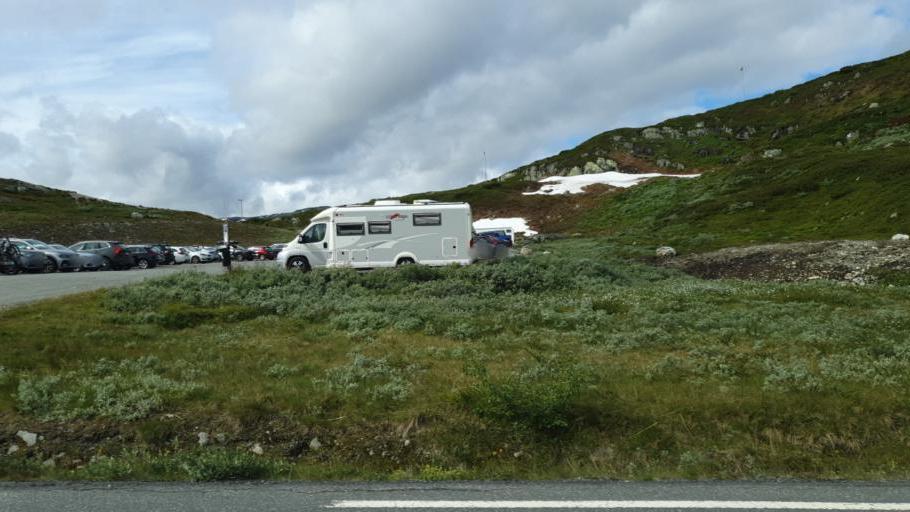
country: NO
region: Oppland
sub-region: Vestre Slidre
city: Slidre
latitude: 61.3189
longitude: 8.8065
